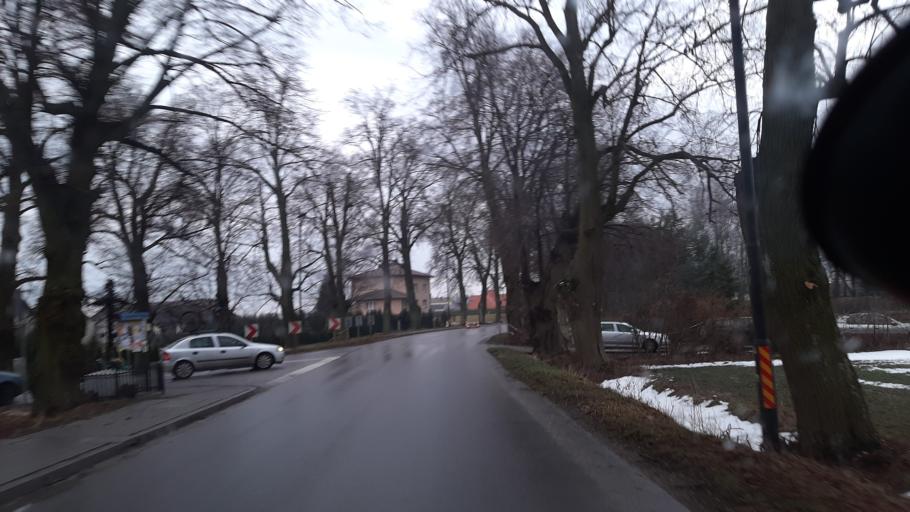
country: PL
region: Lublin Voivodeship
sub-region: Powiat lubelski
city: Lublin
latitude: 51.3256
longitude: 22.5602
